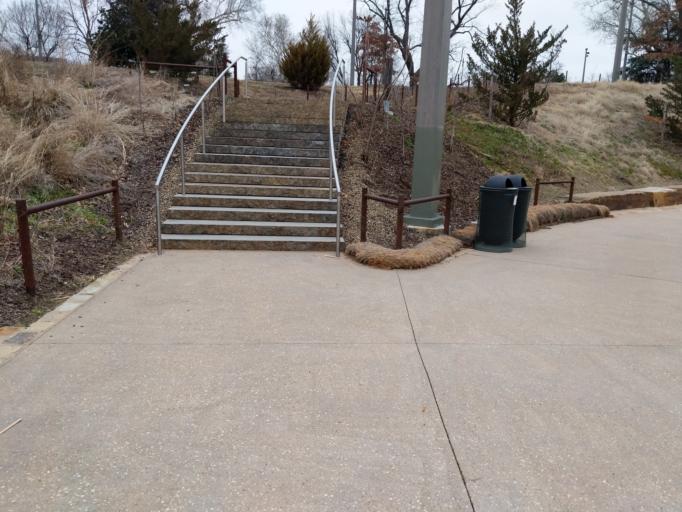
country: US
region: Oklahoma
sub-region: Tulsa County
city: Tulsa
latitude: 36.1251
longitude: -95.9851
